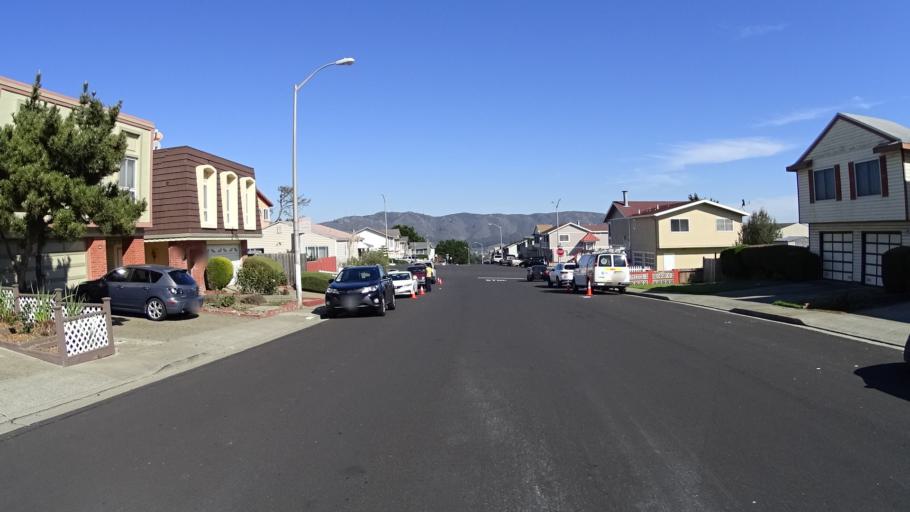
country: US
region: California
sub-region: San Mateo County
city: Colma
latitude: 37.6524
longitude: -122.4600
